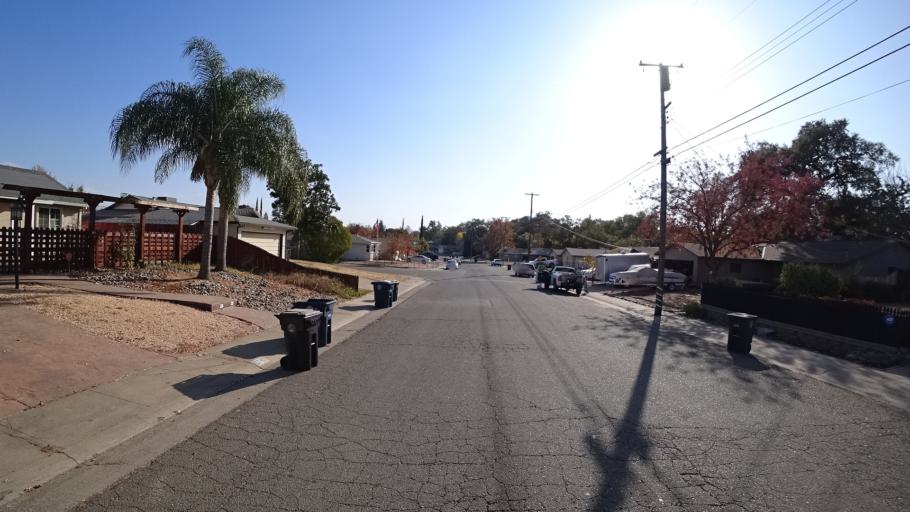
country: US
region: California
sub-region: Sacramento County
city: Citrus Heights
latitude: 38.6890
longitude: -121.2806
